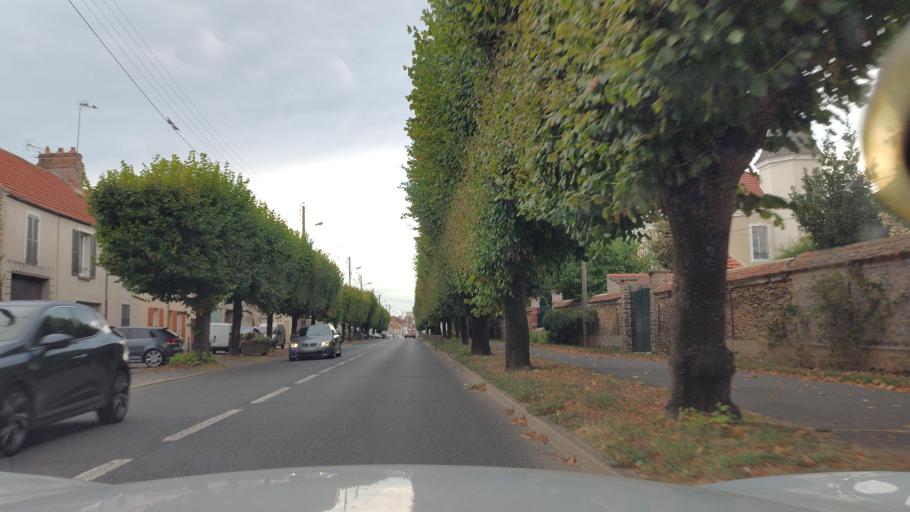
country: FR
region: Ile-de-France
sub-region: Departement de Seine-et-Marne
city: Guignes
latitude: 48.6340
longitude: 2.8030
